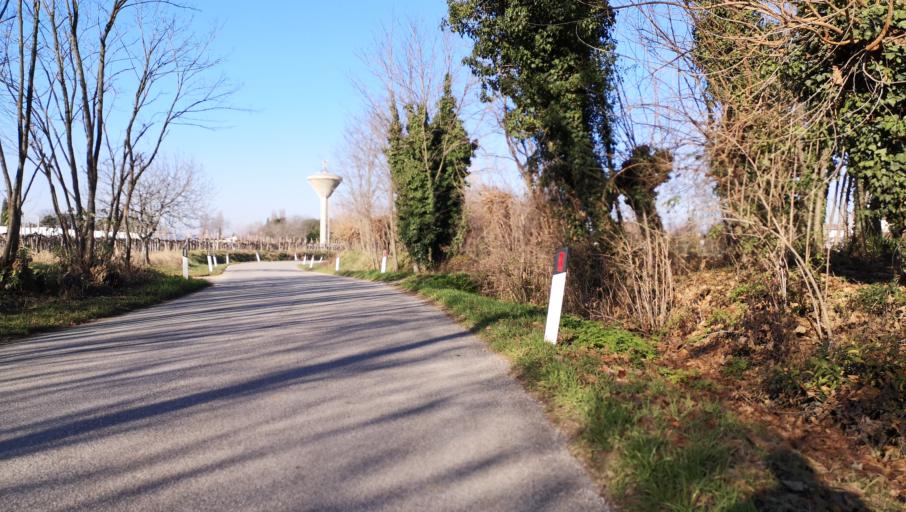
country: IT
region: Friuli Venezia Giulia
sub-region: Provincia di Udine
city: Bicinicco
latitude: 45.9521
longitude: 13.2691
